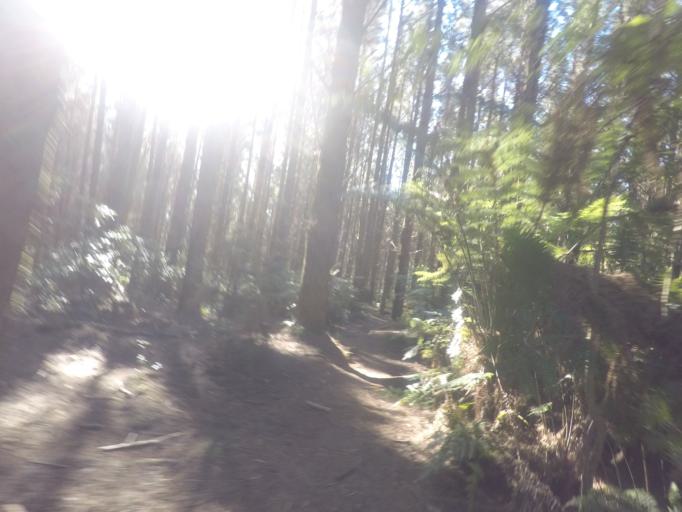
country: NZ
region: Auckland
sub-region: Auckland
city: Muriwai Beach
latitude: -36.7542
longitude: 174.5639
